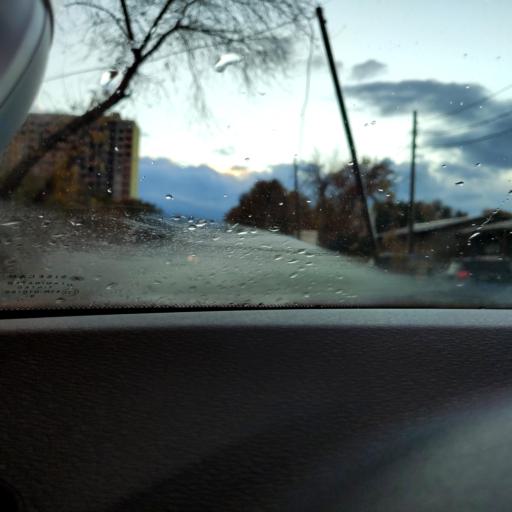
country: RU
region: Samara
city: Smyshlyayevka
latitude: 53.2035
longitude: 50.2858
